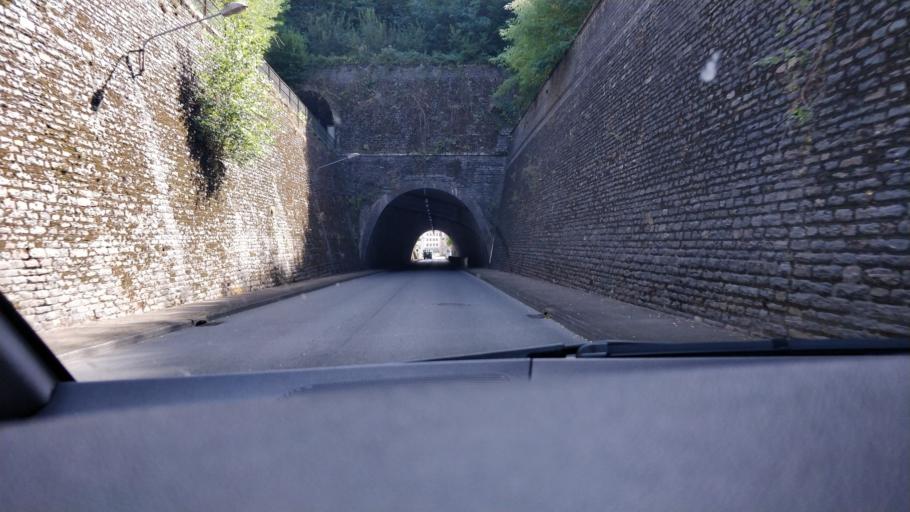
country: FR
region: Limousin
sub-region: Departement de la Correze
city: Uzerche
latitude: 45.4307
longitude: 1.5660
